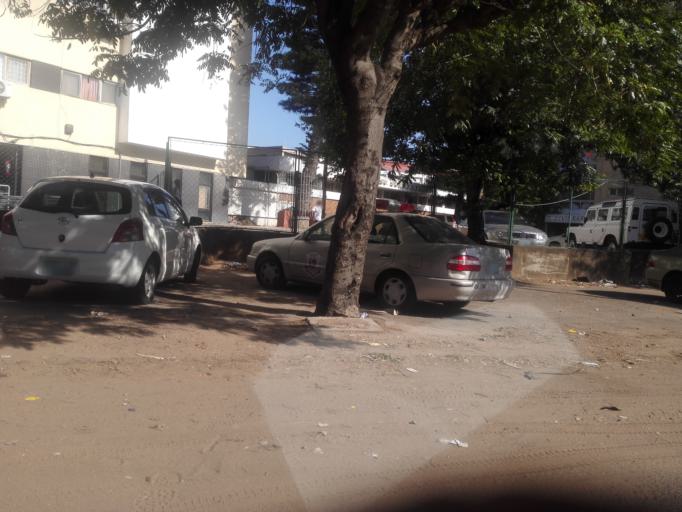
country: MZ
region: Maputo City
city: Maputo
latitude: -25.9558
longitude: 32.5866
